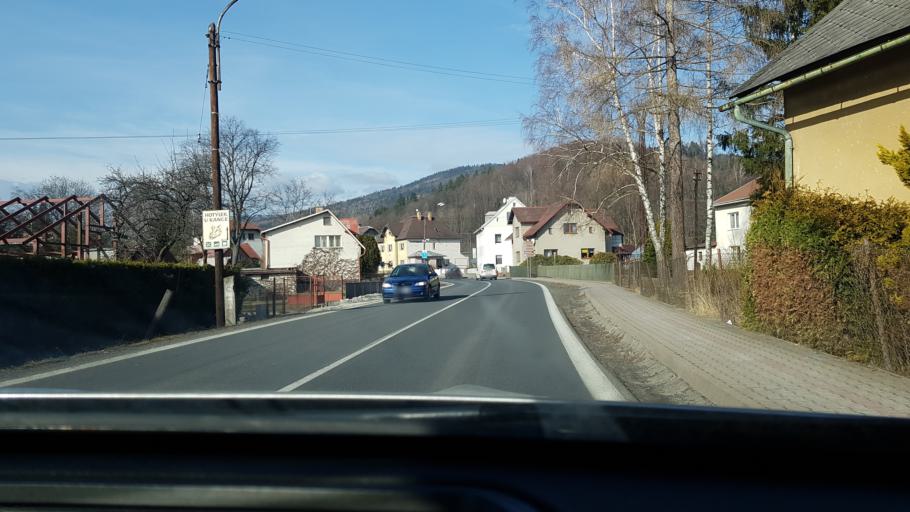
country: CZ
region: Olomoucky
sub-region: Okres Jesenik
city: Jesenik
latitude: 50.2289
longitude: 17.1541
